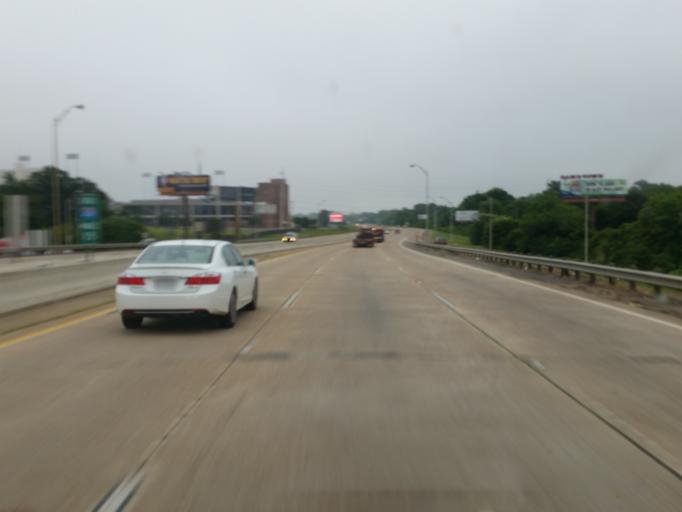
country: US
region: Louisiana
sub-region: Caddo Parish
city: Shreveport
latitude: 32.4723
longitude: -93.7971
